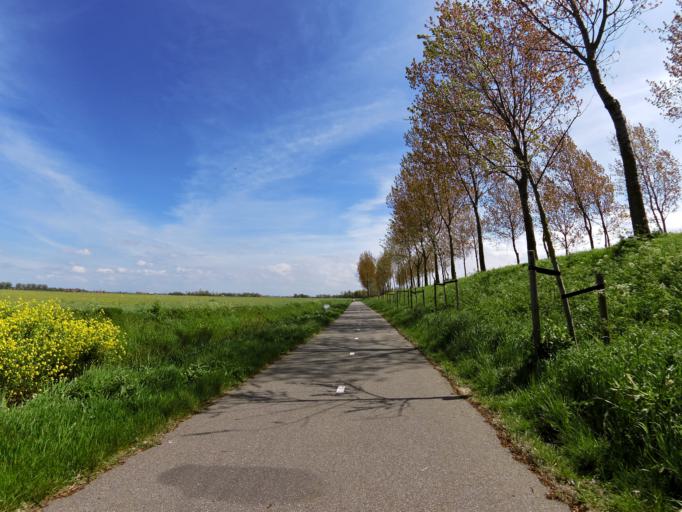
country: NL
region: South Holland
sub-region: Gemeente Hellevoetsluis
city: Nieuw-Helvoet
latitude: 51.8704
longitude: 4.1000
